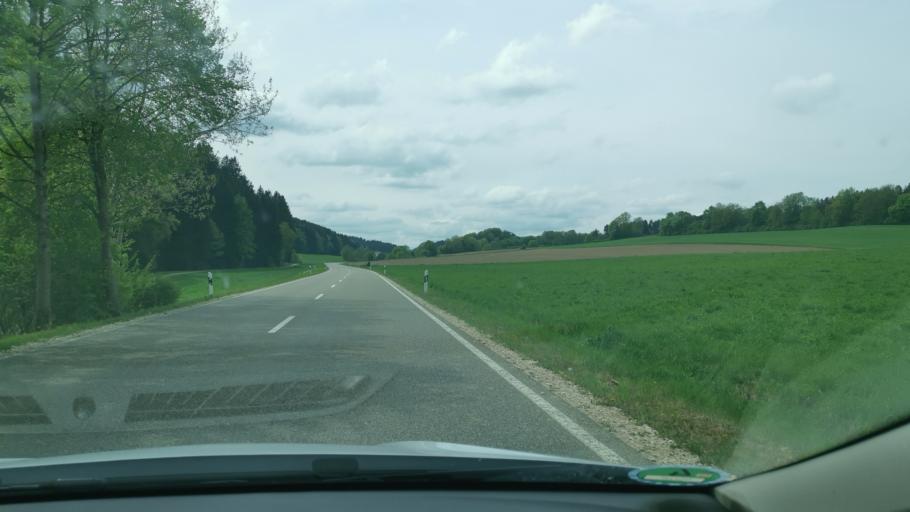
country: DE
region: Bavaria
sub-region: Swabia
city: Schiltberg
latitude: 48.4536
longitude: 11.2268
